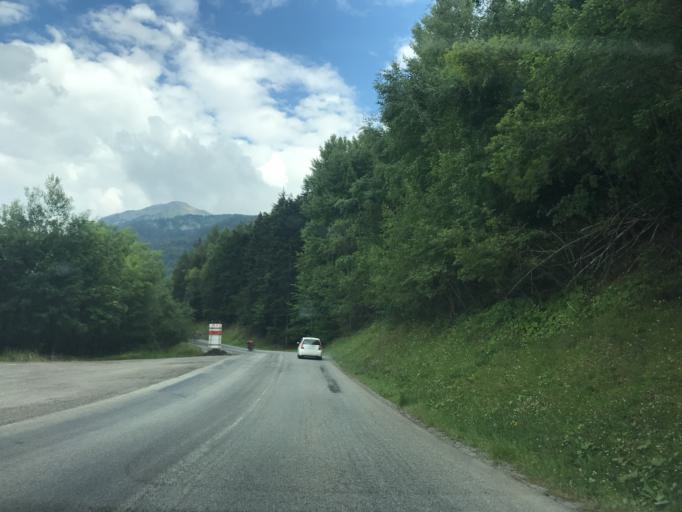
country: FR
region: Rhone-Alpes
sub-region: Departement de la Savoie
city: Saint-Michel-de-Maurienne
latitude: 45.2024
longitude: 6.4641
